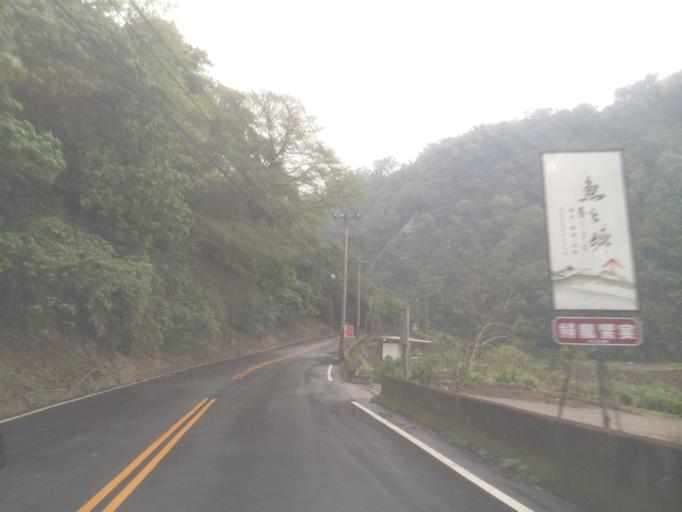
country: TW
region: Taiwan
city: Fengyuan
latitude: 24.1678
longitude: 120.8269
